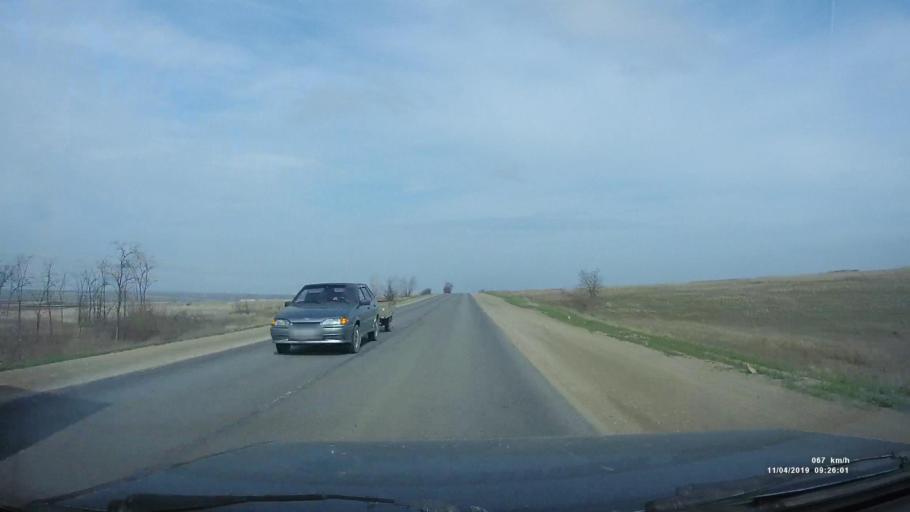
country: RU
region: Rostov
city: Staraya Stanitsa
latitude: 48.2607
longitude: 40.3673
